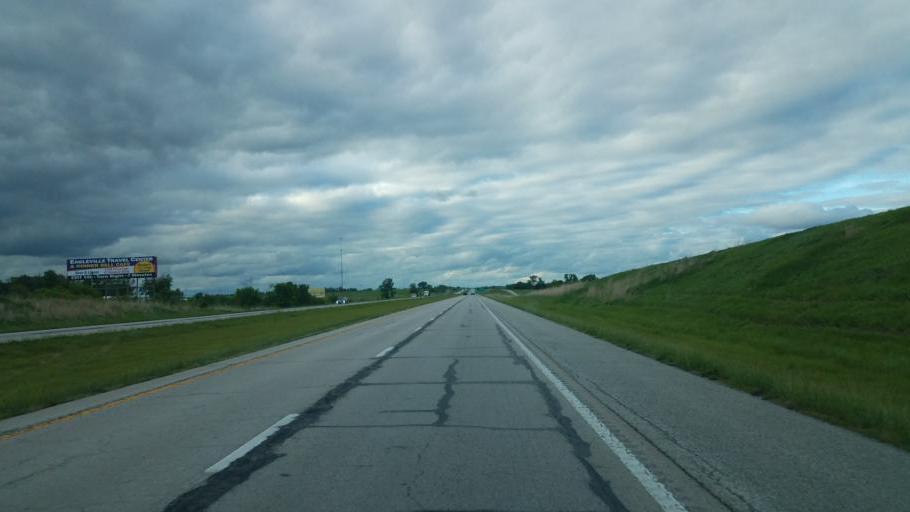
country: US
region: Missouri
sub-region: Harrison County
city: Bethany
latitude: 40.3489
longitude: -94.0097
